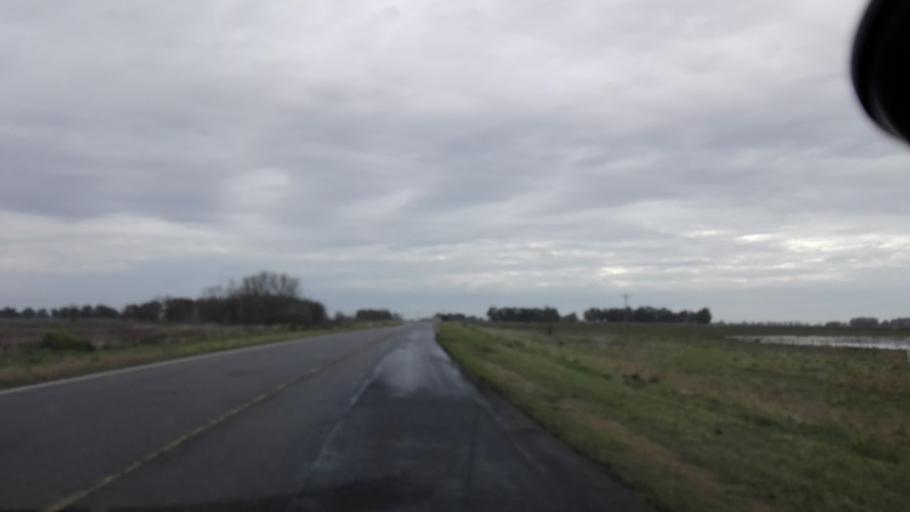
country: AR
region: Buenos Aires
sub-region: Partido de Rauch
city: Rauch
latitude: -36.6129
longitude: -59.0601
